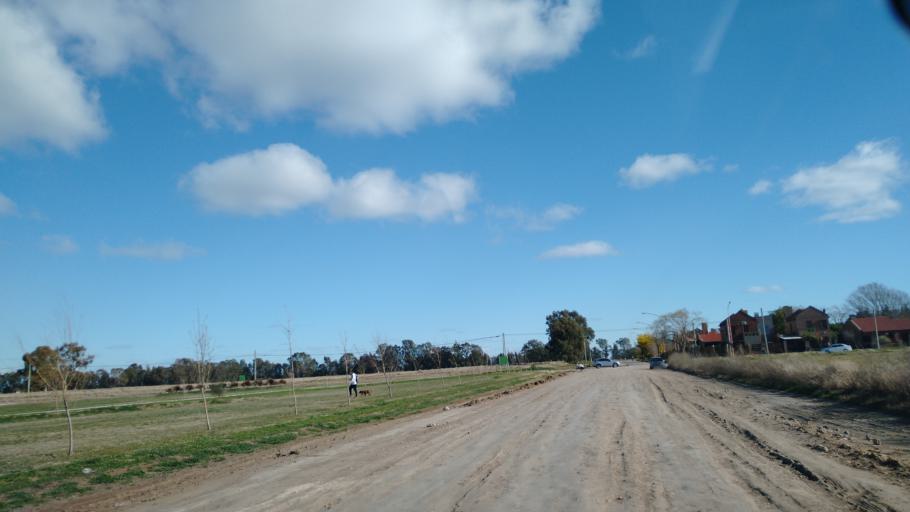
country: AR
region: Buenos Aires
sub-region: Partido de Bahia Blanca
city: Bahia Blanca
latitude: -38.7094
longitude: -62.2049
